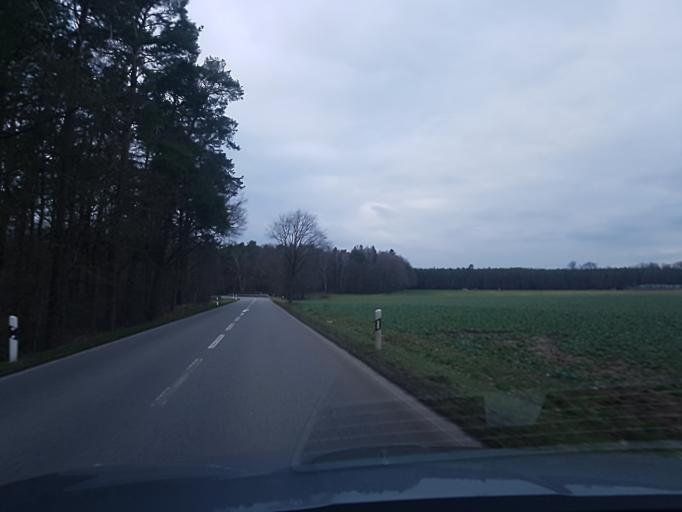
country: DE
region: Brandenburg
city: Finsterwalde
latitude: 51.6741
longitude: 13.6906
